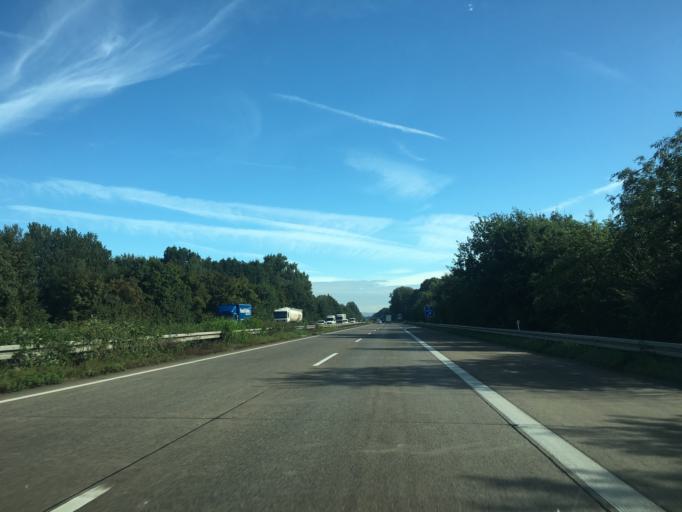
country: DE
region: North Rhine-Westphalia
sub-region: Regierungsbezirk Munster
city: Ladbergen
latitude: 52.1289
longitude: 7.7175
